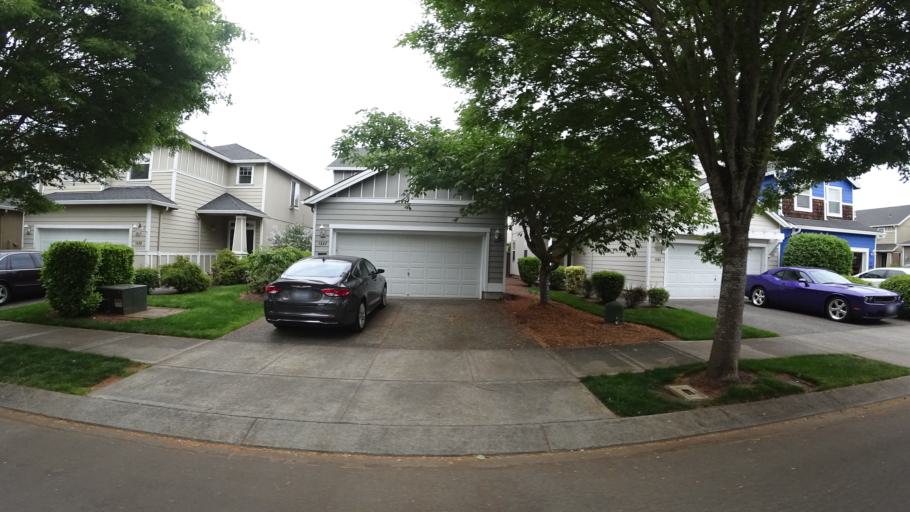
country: US
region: Oregon
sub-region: Washington County
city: Hillsboro
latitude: 45.4953
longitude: -122.9672
